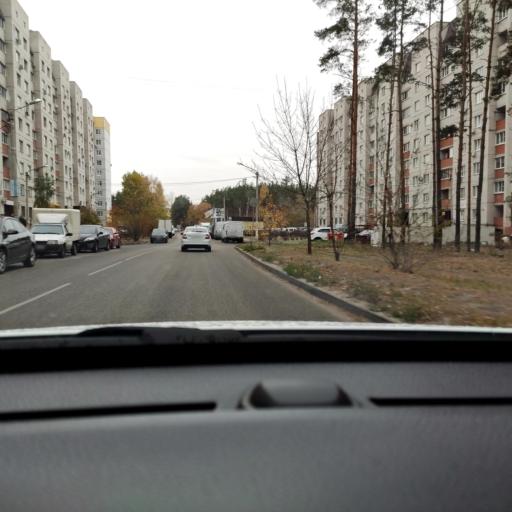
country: RU
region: Voronezj
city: Voronezh
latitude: 51.6888
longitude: 39.2790
